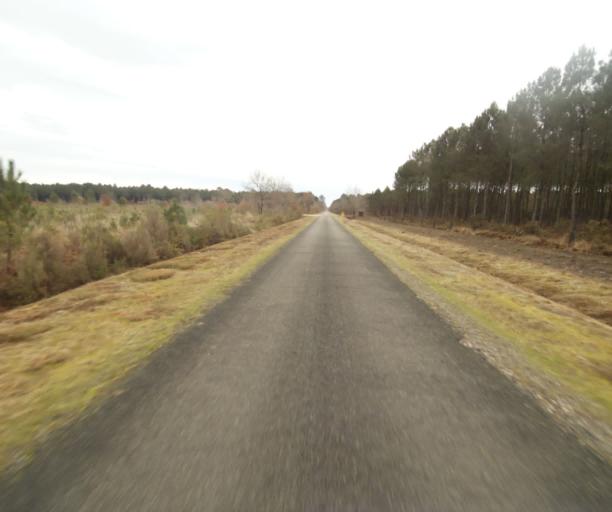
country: FR
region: Aquitaine
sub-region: Departement des Landes
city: Gabarret
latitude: 44.0265
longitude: -0.0542
